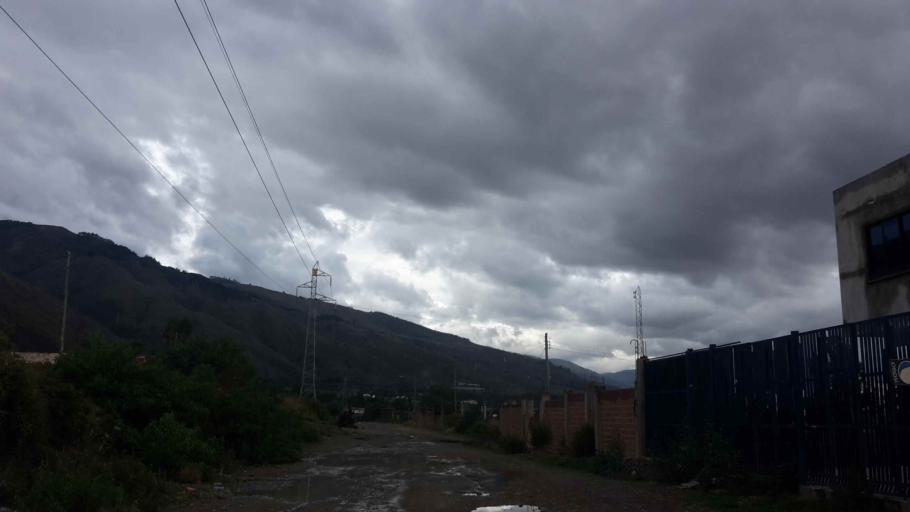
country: BO
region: Cochabamba
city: Cochabamba
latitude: -17.3781
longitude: -66.0614
